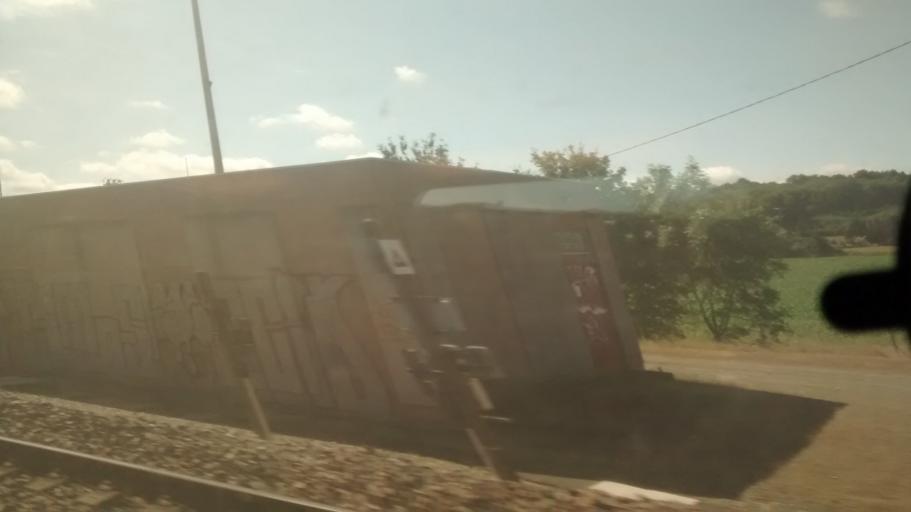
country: FR
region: Pays de la Loire
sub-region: Departement de la Sarthe
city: Dollon
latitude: 48.0471
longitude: 0.5622
